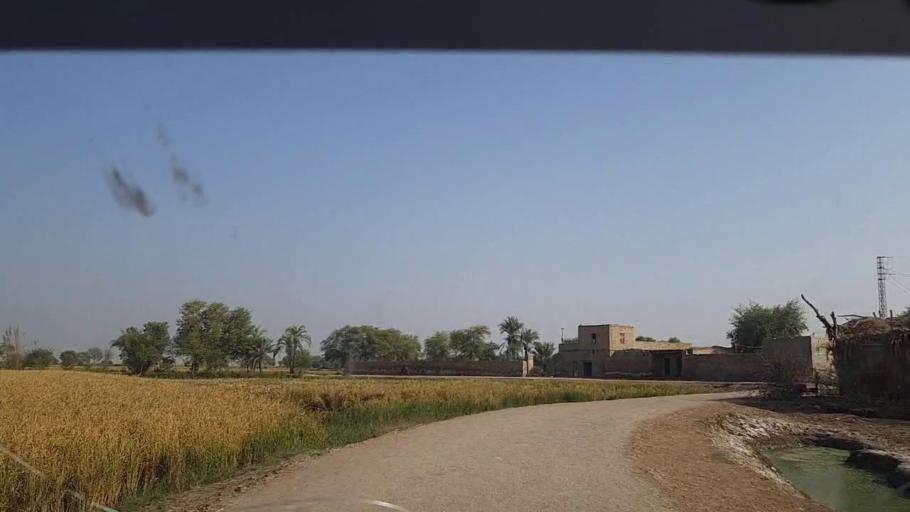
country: PK
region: Sindh
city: Shikarpur
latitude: 28.1169
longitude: 68.5806
